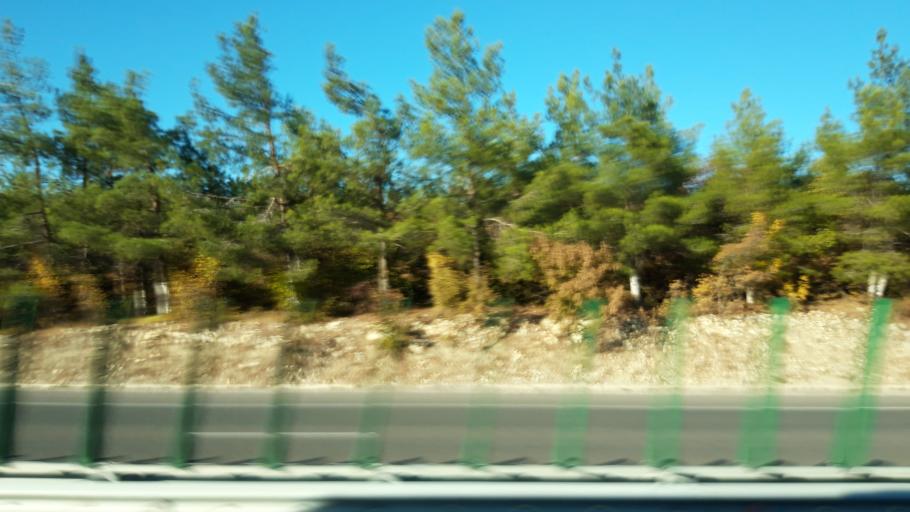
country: RU
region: Krasnodarskiy
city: Kabardinka
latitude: 44.6403
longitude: 37.9814
